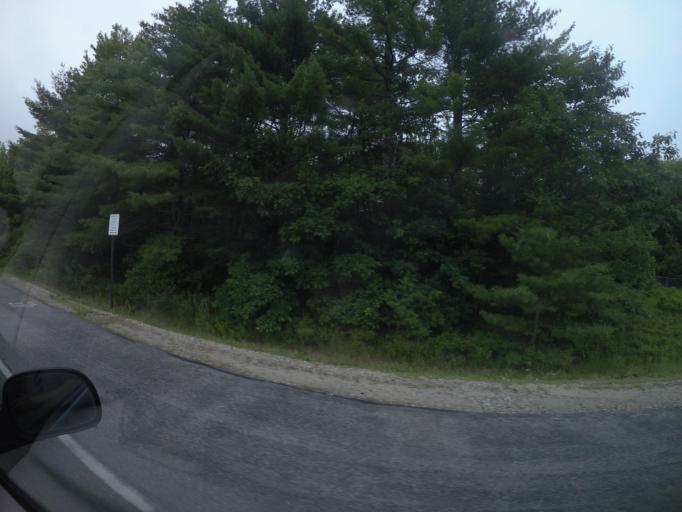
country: US
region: Maine
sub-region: York County
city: Biddeford
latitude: 43.4762
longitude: -70.4946
